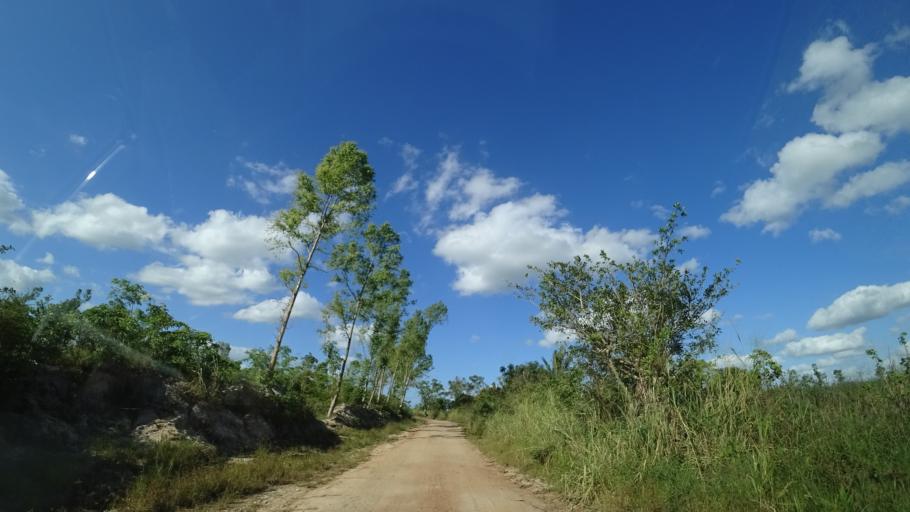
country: MZ
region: Sofala
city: Dondo
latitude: -19.4238
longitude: 34.7102
